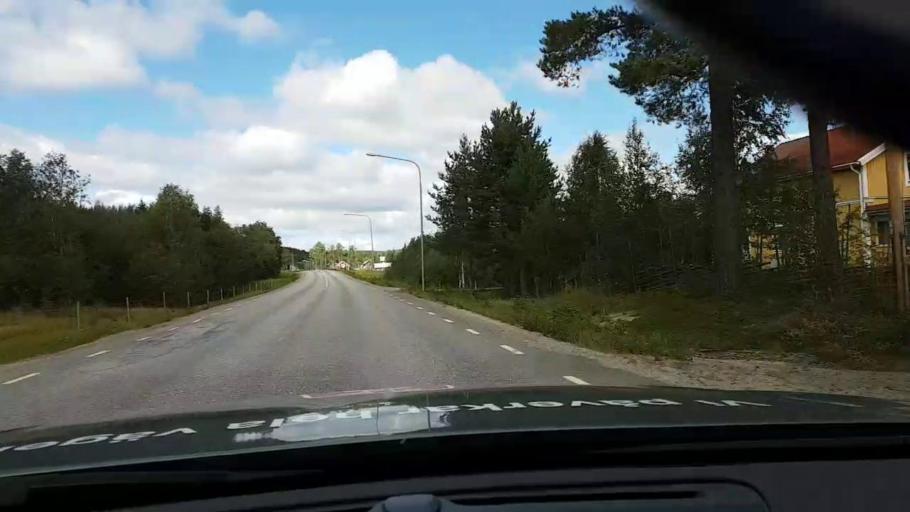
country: SE
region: Vaesternorrland
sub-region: OErnskoeldsviks Kommun
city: Bredbyn
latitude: 63.4778
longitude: 18.0937
